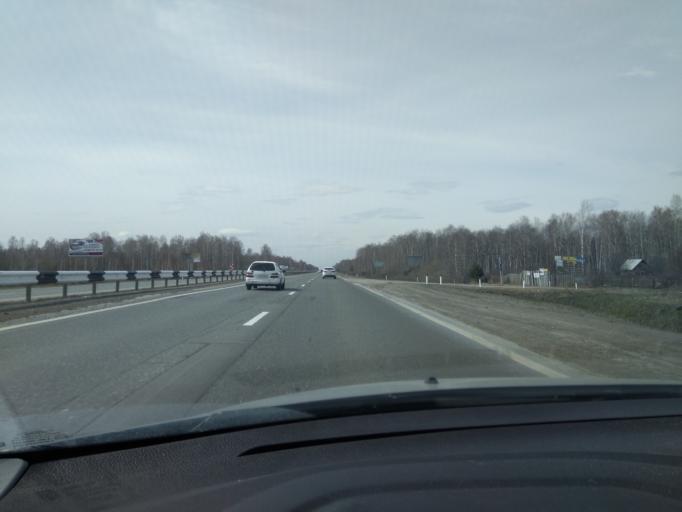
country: RU
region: Tjumen
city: Moskovskiy
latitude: 57.1114
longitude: 65.3932
